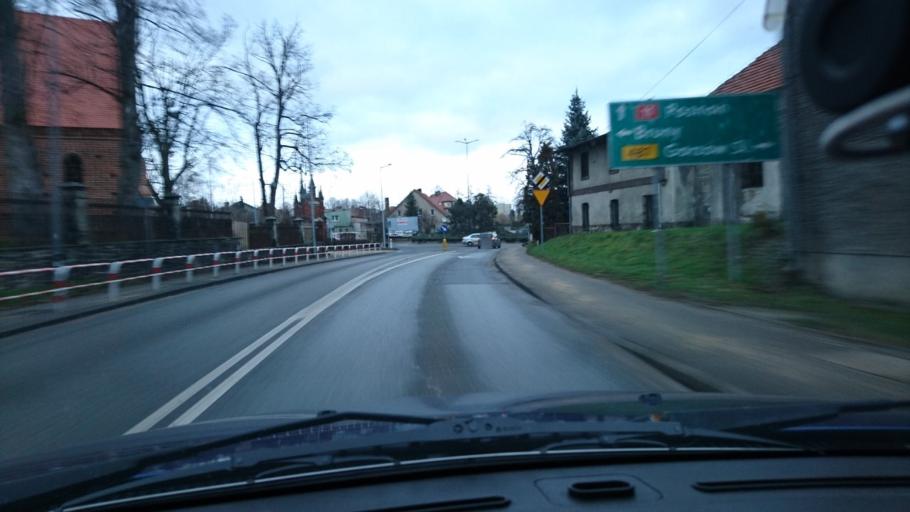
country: PL
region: Opole Voivodeship
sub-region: Powiat kluczborski
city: Byczyna
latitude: 51.1125
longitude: 18.2084
